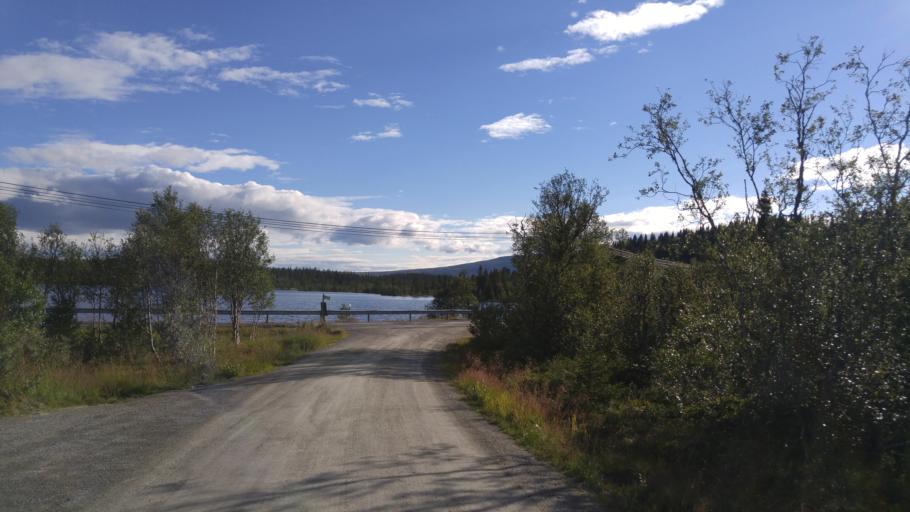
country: NO
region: Buskerud
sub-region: Hemsedal
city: Troim
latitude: 60.8462
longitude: 8.7234
